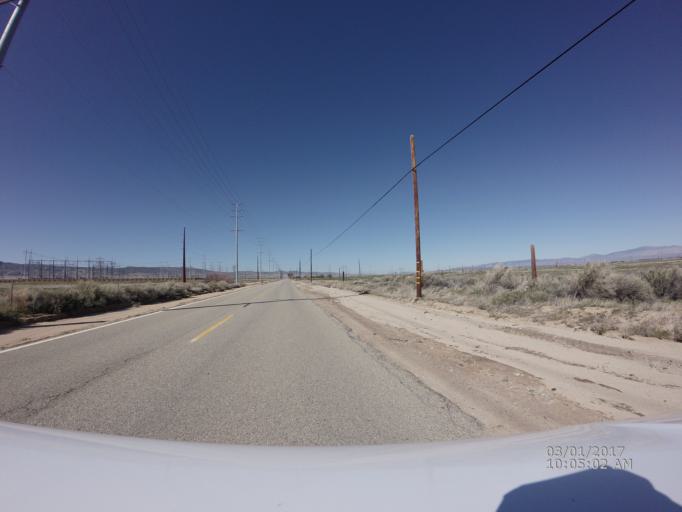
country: US
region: California
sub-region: Los Angeles County
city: Leona Valley
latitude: 34.6893
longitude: -118.2924
